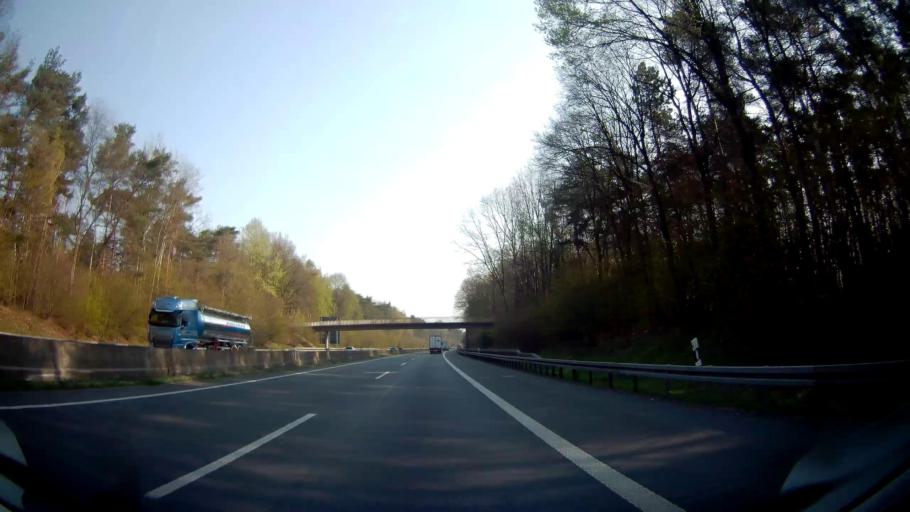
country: DE
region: North Rhine-Westphalia
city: Marl
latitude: 51.6609
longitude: 7.0529
